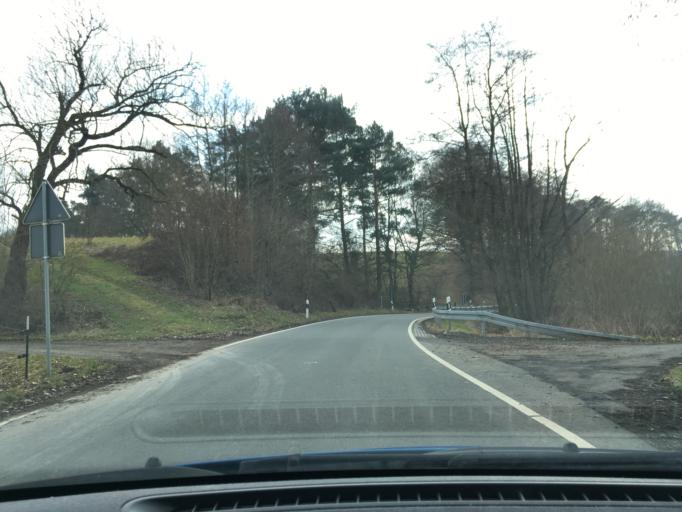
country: DE
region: Lower Saxony
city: Adelebsen
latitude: 51.5880
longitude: 9.6811
